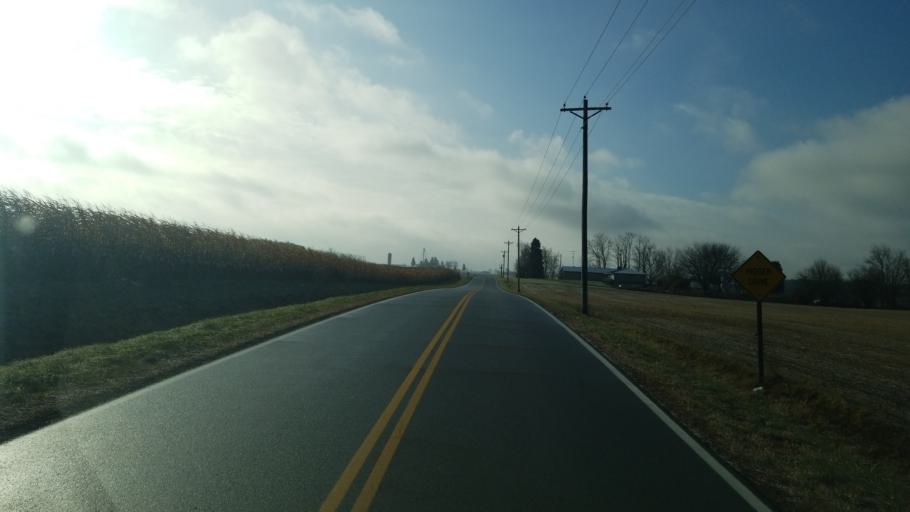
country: US
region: Ohio
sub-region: Richland County
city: Shelby
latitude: 40.9119
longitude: -82.7434
